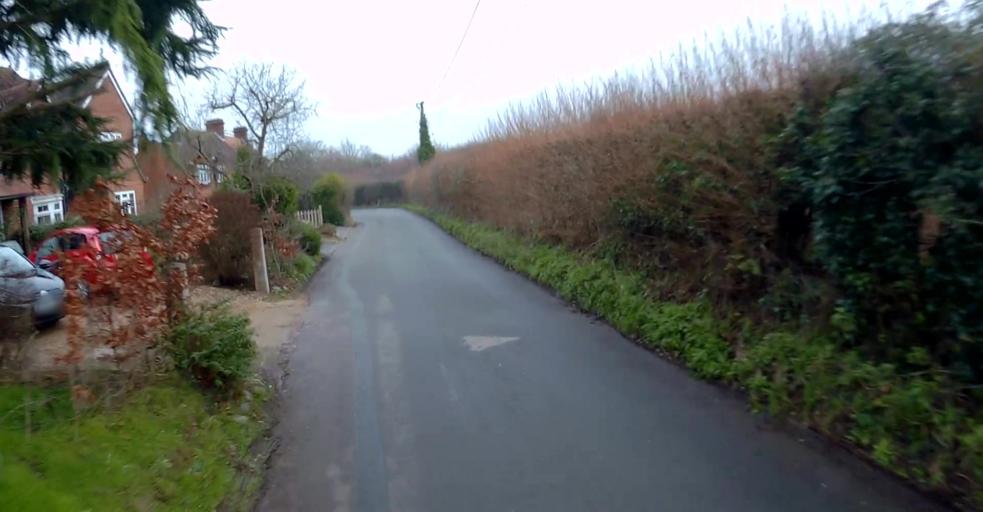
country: GB
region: England
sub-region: Hampshire
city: Old Basing
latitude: 51.2764
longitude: -1.0520
